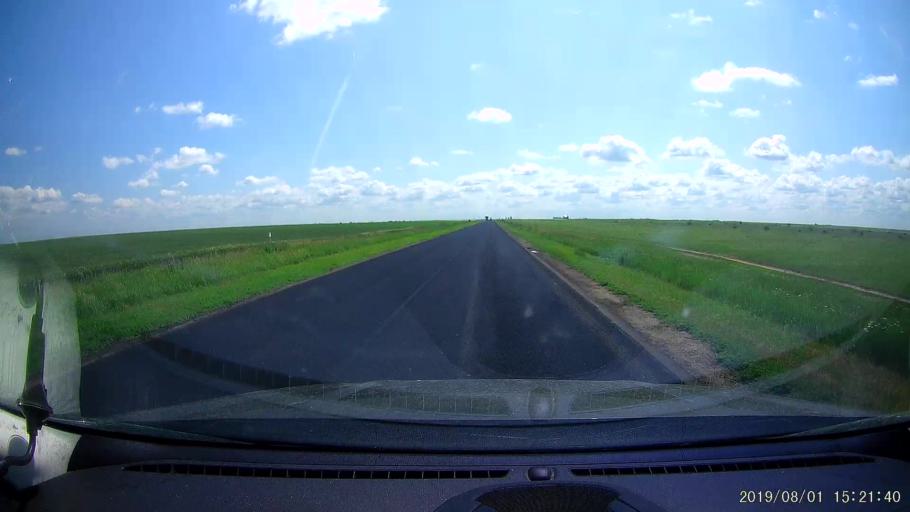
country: RO
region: Braila
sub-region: Comuna Tufesti
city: Tufesti
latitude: 45.0663
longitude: 27.7917
